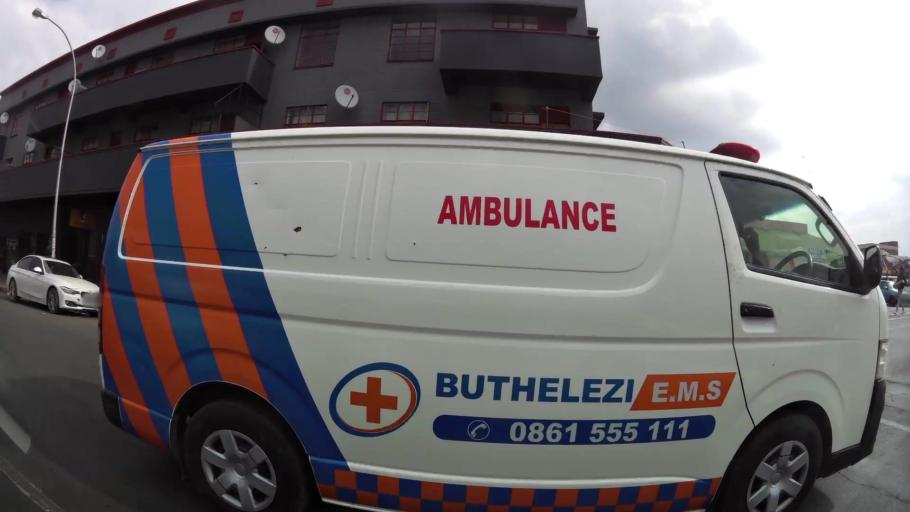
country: ZA
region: Orange Free State
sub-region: Mangaung Metropolitan Municipality
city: Bloemfontein
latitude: -29.1168
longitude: 26.2254
